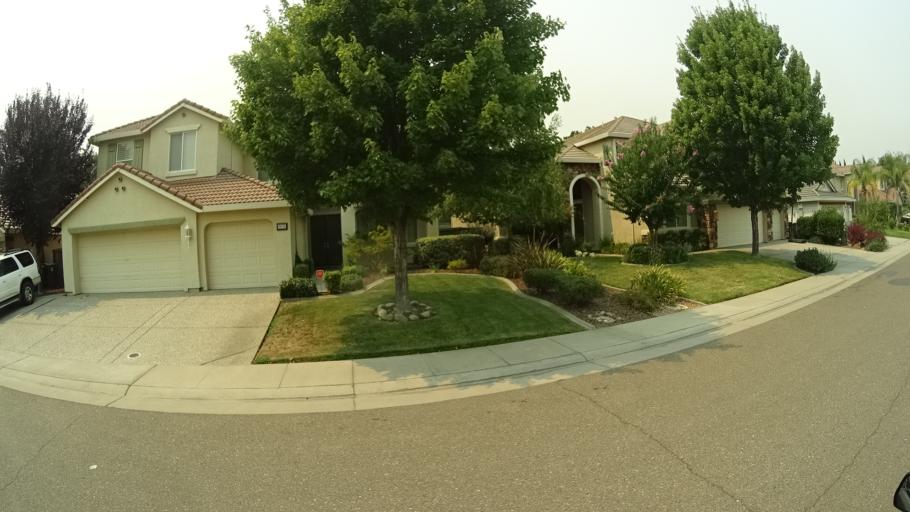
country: US
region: California
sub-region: Sacramento County
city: Laguna
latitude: 38.4075
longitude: -121.4238
